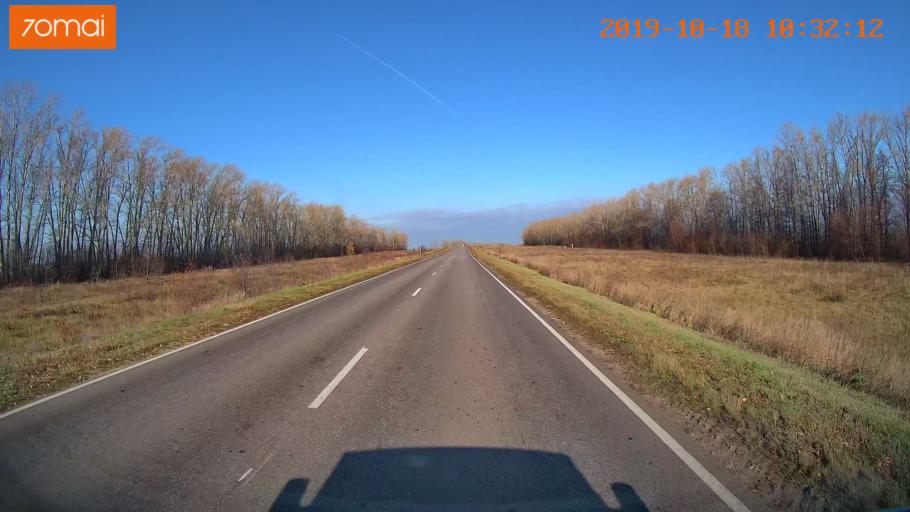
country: RU
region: Tula
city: Kurkino
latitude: 53.4907
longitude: 38.6256
